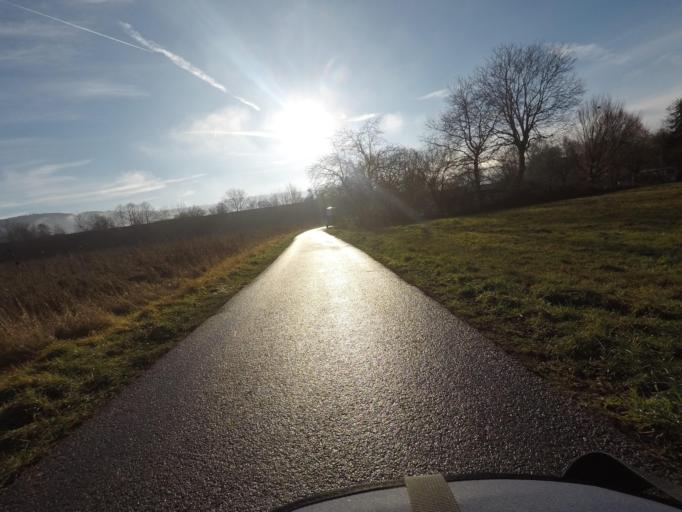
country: DE
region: Baden-Wuerttemberg
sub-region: Karlsruhe Region
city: Ettlingen
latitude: 48.9663
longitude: 8.4190
